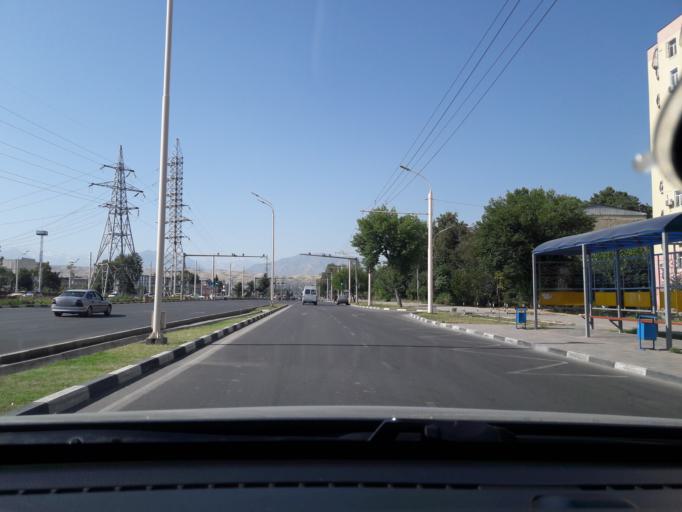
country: TJ
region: Dushanbe
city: Dushanbe
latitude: 38.5561
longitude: 68.7416
